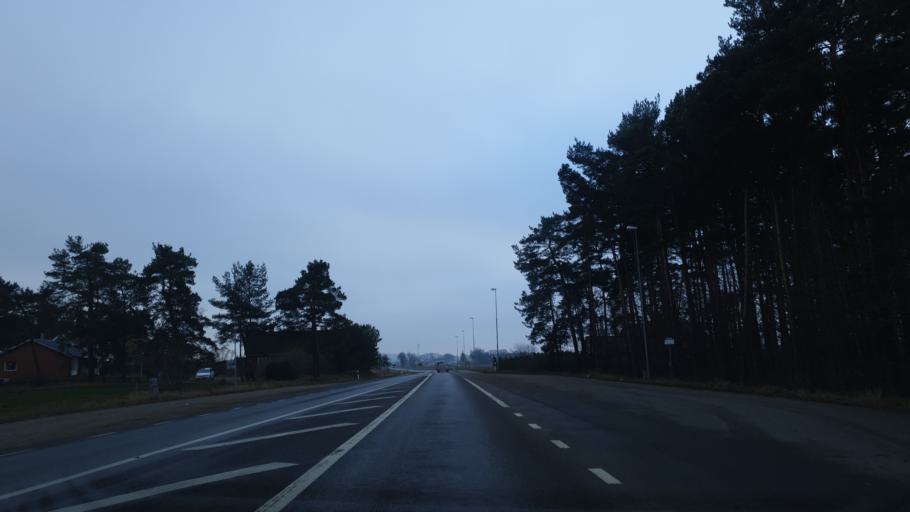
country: SE
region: Blekinge
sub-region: Solvesborgs Kommun
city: Soelvesborg
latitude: 56.0864
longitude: 14.6477
